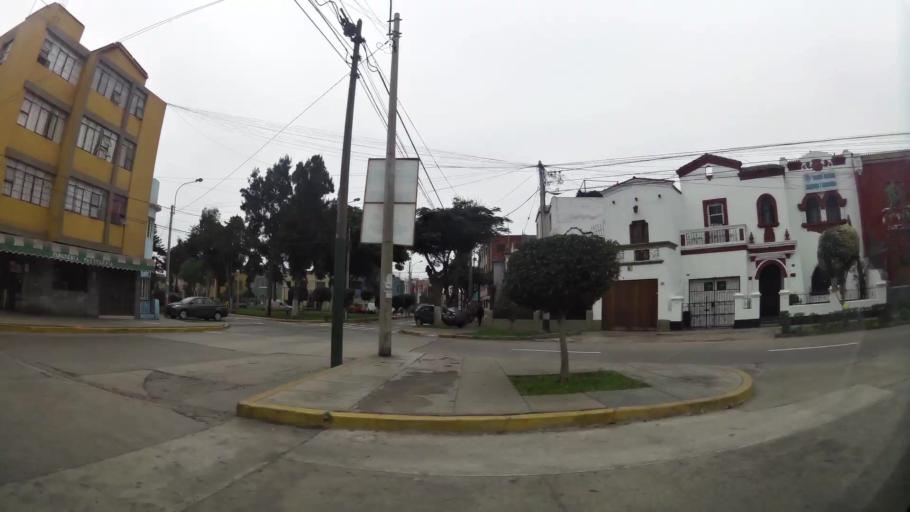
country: PE
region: Lima
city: Lima
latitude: -12.0762
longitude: -77.0444
